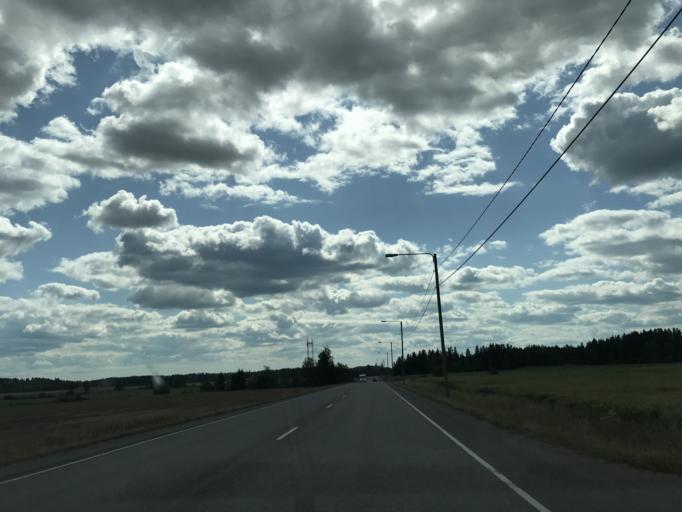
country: FI
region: Uusimaa
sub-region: Helsinki
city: Maentsaelae
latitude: 60.6597
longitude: 25.3470
